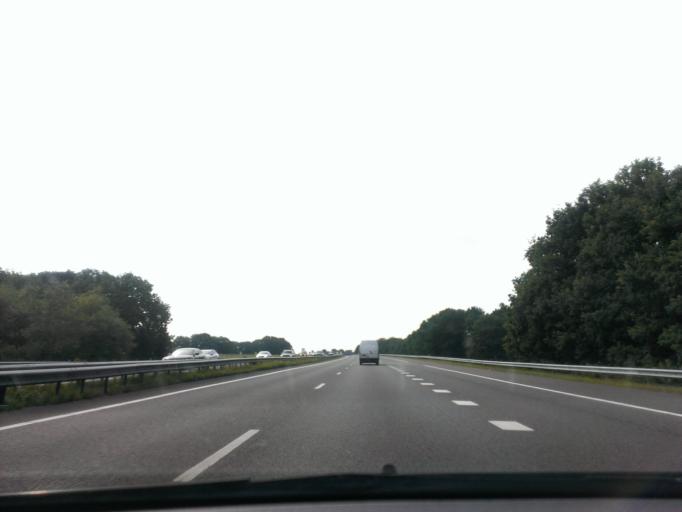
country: NL
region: Gelderland
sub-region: Gemeente Barneveld
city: Stroe
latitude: 52.1918
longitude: 5.7015
